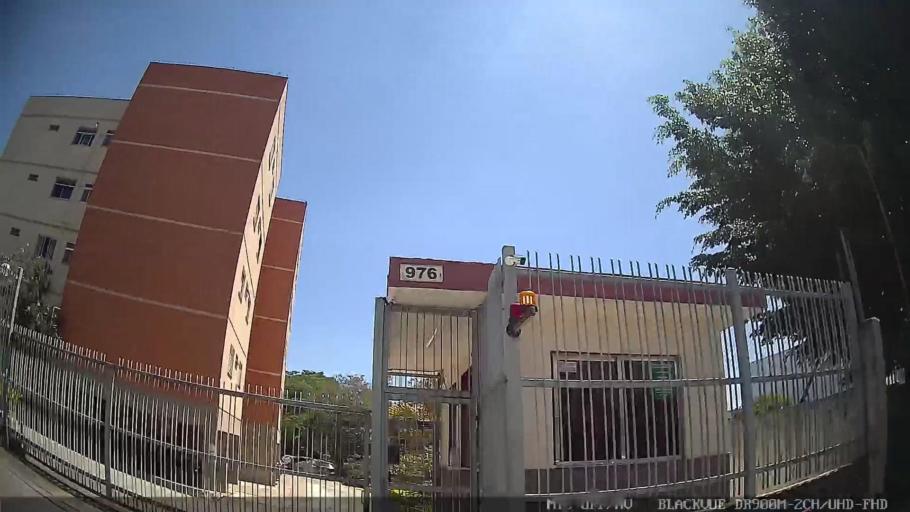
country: BR
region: Sao Paulo
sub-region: Sao Caetano Do Sul
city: Sao Caetano do Sul
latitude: -23.6000
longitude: -46.5479
